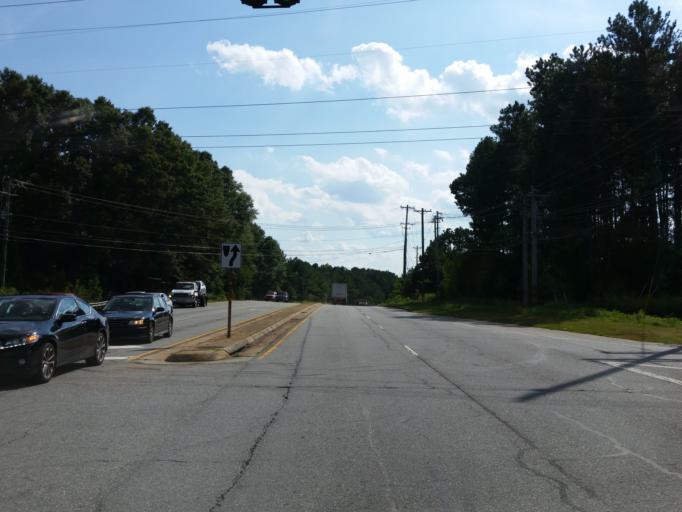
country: US
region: Georgia
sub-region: Gwinnett County
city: Lawrenceville
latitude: 33.9565
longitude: -84.0179
